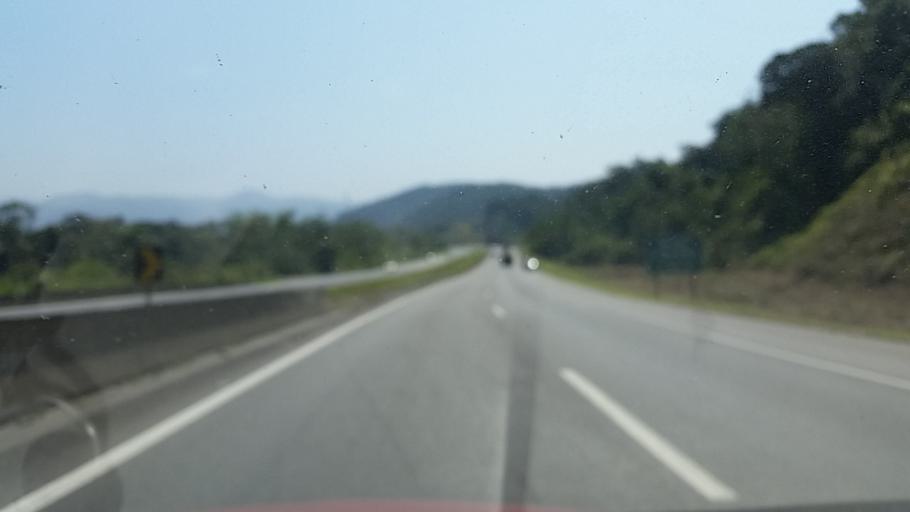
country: BR
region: Sao Paulo
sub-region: Miracatu
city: Miracatu
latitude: -24.2253
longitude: -47.3645
